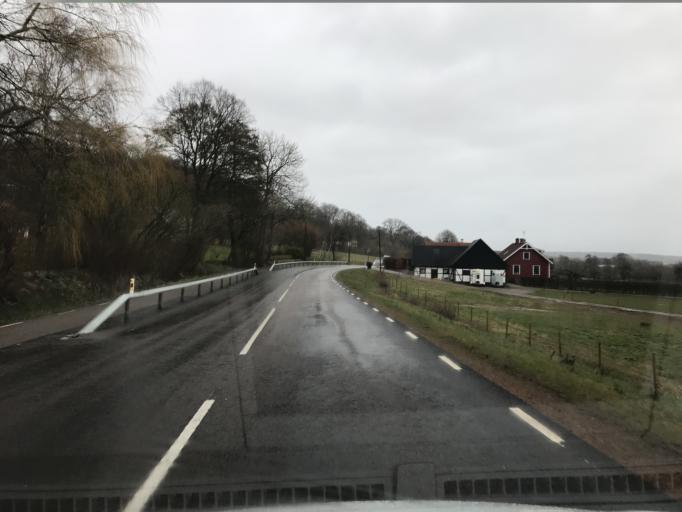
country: SE
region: Skane
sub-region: Bastads Kommun
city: Forslov
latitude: 56.3474
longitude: 12.8580
